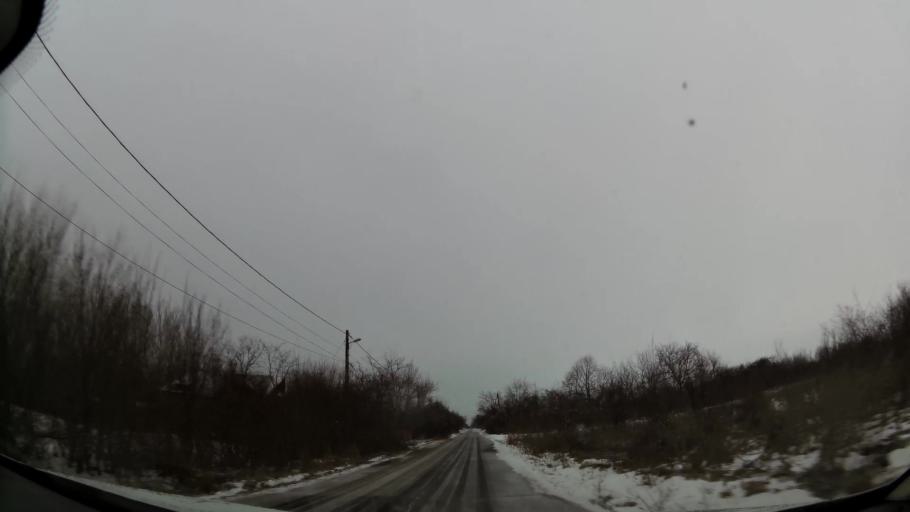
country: RO
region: Prahova
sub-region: Comuna Poenarii-Burchi
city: Ologeni
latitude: 44.7326
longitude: 25.9160
